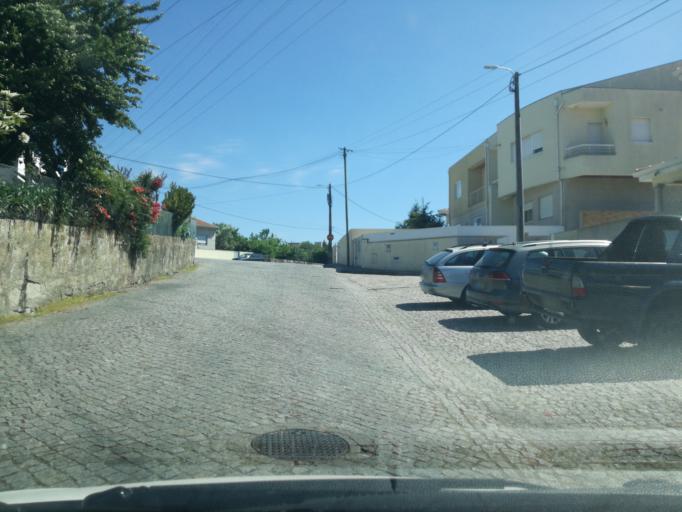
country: PT
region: Porto
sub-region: Maia
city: Anta
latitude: 41.2697
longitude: -8.6325
